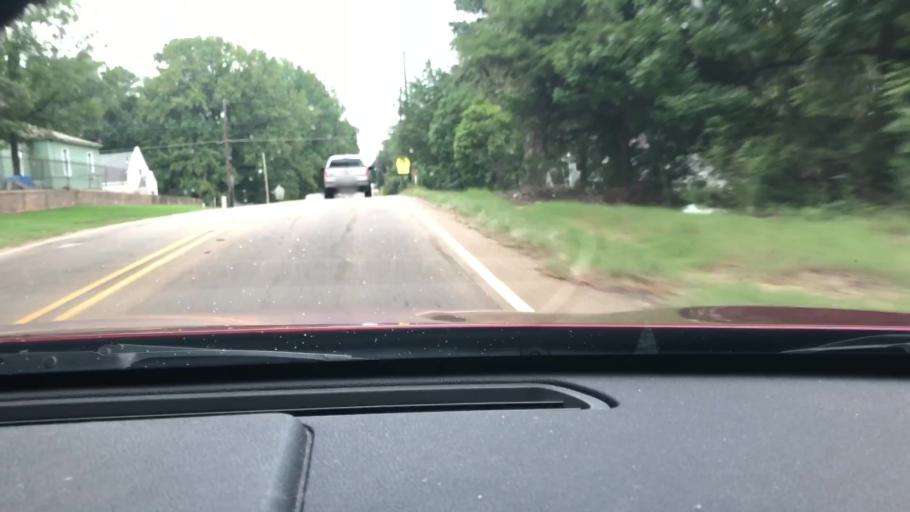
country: US
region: Arkansas
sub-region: Lafayette County
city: Stamps
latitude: 33.3655
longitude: -93.4957
